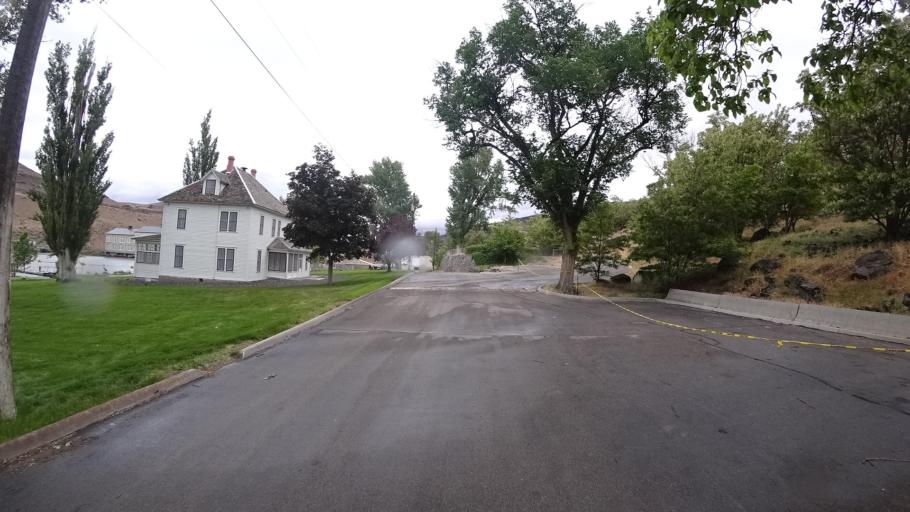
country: US
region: Idaho
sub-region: Owyhee County
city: Murphy
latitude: 43.2427
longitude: -116.3761
